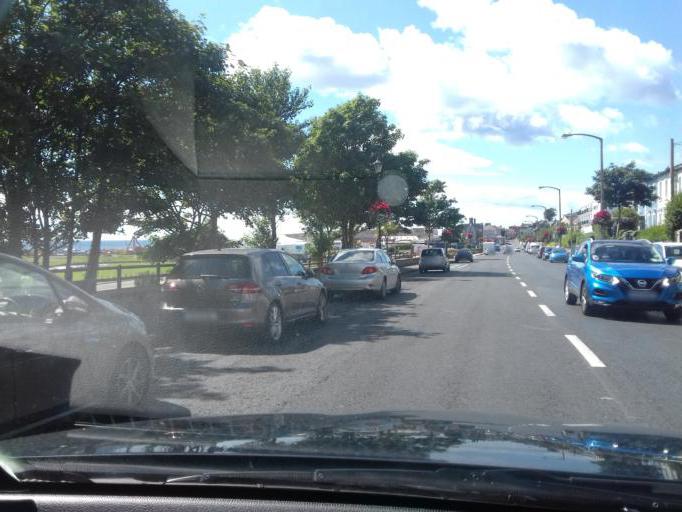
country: IE
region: Munster
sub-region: Waterford
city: Tra Mhor
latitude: 52.1644
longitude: -7.1468
